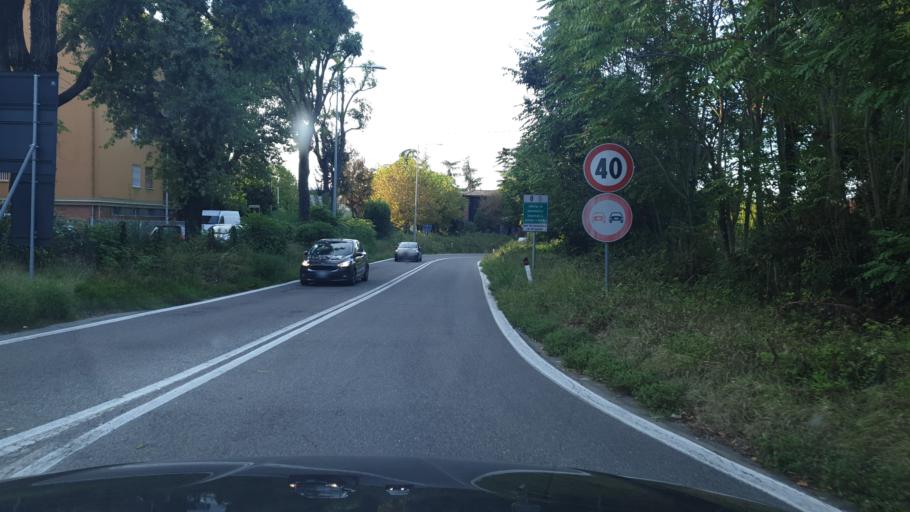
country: IT
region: Emilia-Romagna
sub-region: Provincia di Bologna
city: Quarto Inferiore
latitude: 44.5094
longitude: 11.3796
